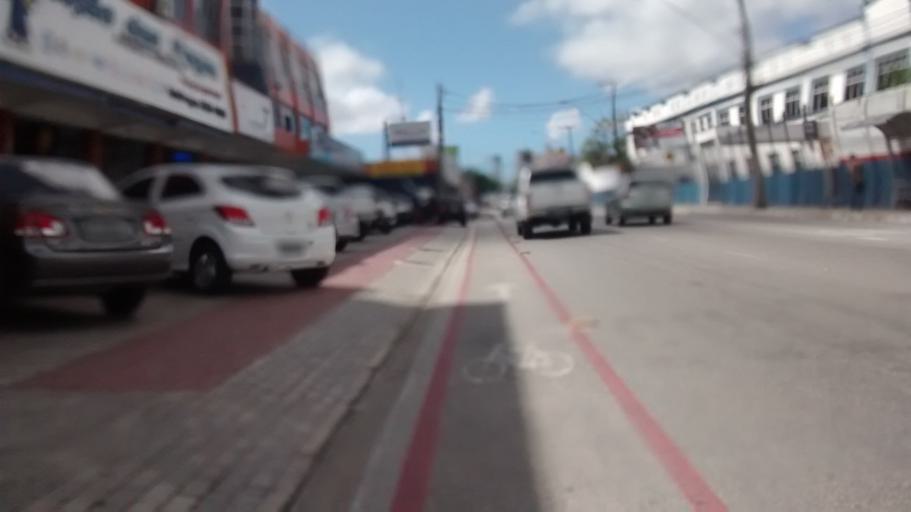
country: BR
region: Ceara
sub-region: Fortaleza
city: Fortaleza
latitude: -3.7395
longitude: -38.5213
